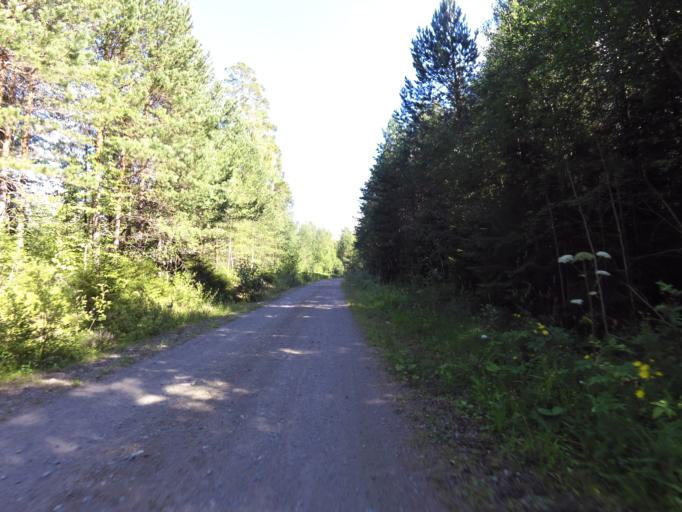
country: SE
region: Gaevleborg
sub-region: Hofors Kommun
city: Hofors
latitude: 60.5098
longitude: 16.3524
